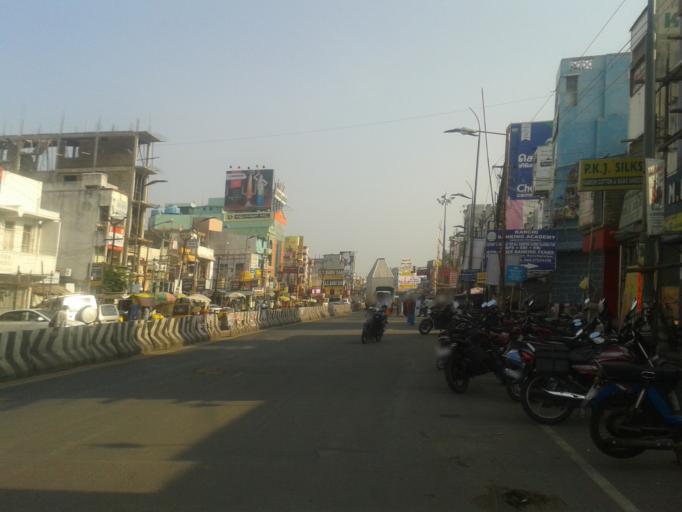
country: IN
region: Tamil Nadu
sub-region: Kancheepuram
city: Kanchipuram
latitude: 12.8275
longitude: 79.7075
